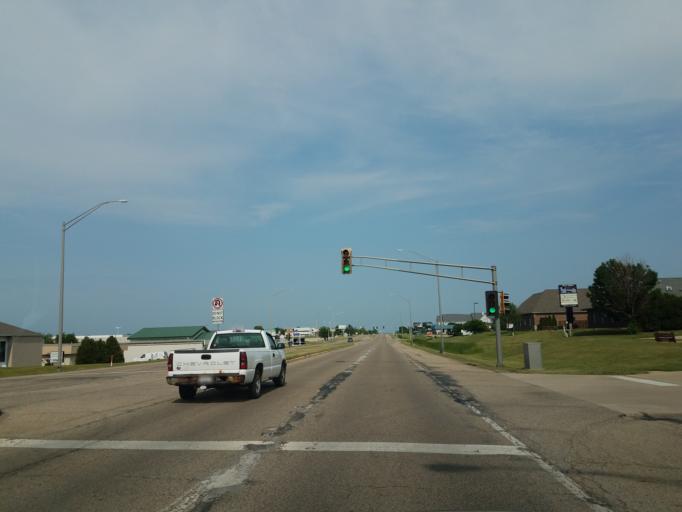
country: US
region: Illinois
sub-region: McLean County
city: Bloomington
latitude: 40.4883
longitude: -88.9415
